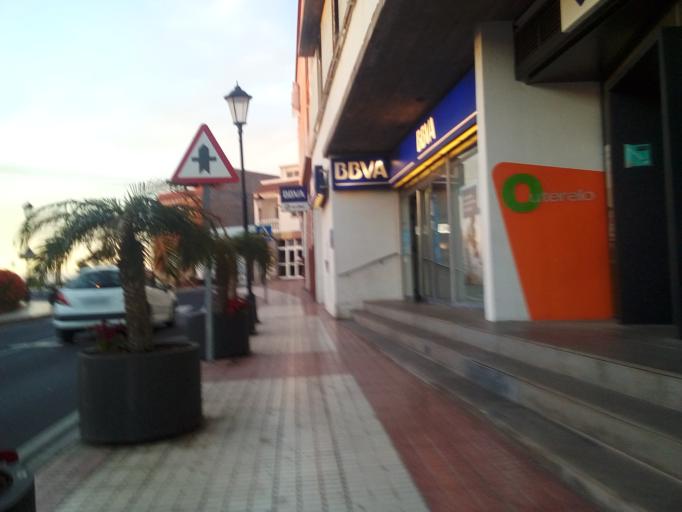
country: ES
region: Canary Islands
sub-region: Provincia de Santa Cruz de Tenerife
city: Alajero
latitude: 28.0880
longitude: -17.3355
